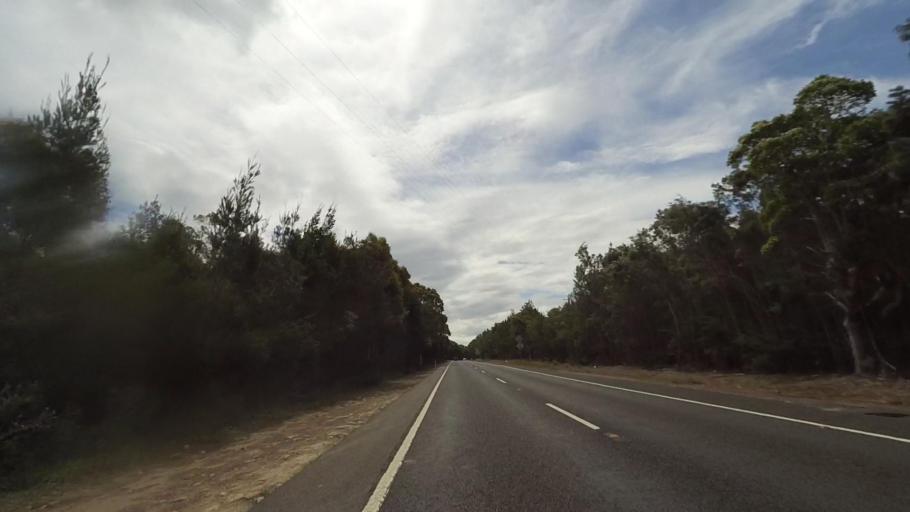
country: AU
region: New South Wales
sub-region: Sutherland Shire
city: Loftus
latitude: -34.0595
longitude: 151.0523
